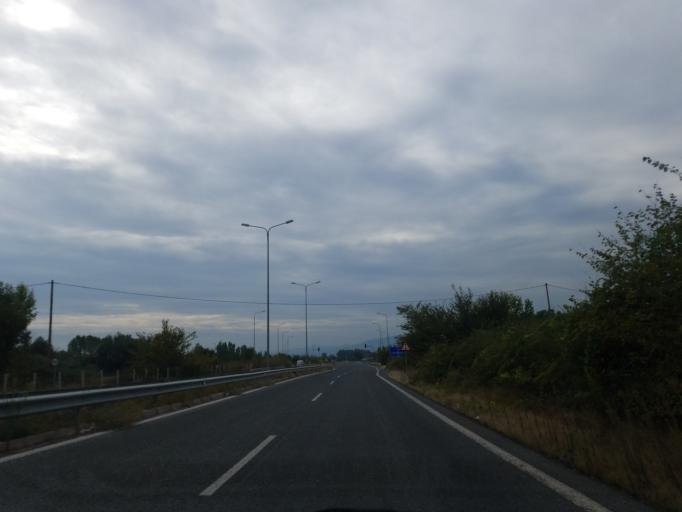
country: GR
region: Thessaly
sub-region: Trikala
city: Pyrgetos
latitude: 39.5428
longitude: 21.7354
